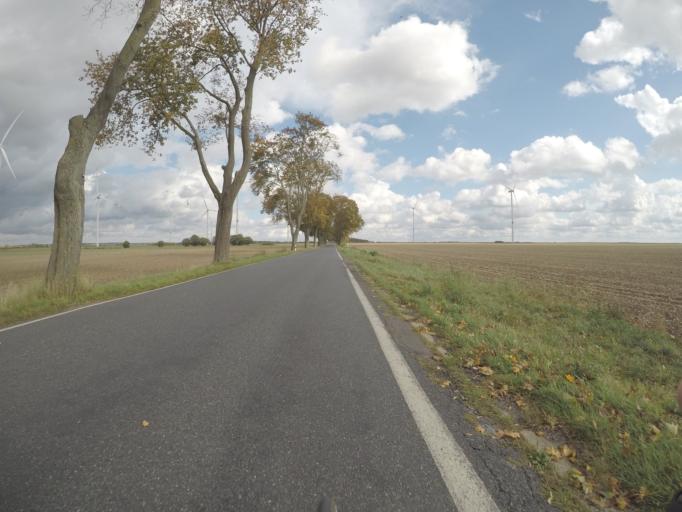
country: DE
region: Brandenburg
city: Werneuchen
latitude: 52.6031
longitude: 13.7764
